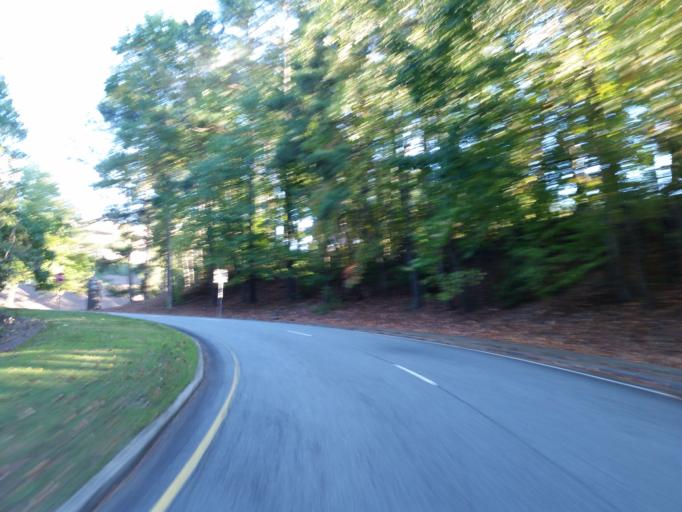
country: US
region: Georgia
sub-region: Cobb County
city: Vinings
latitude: 33.8703
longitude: -84.4731
